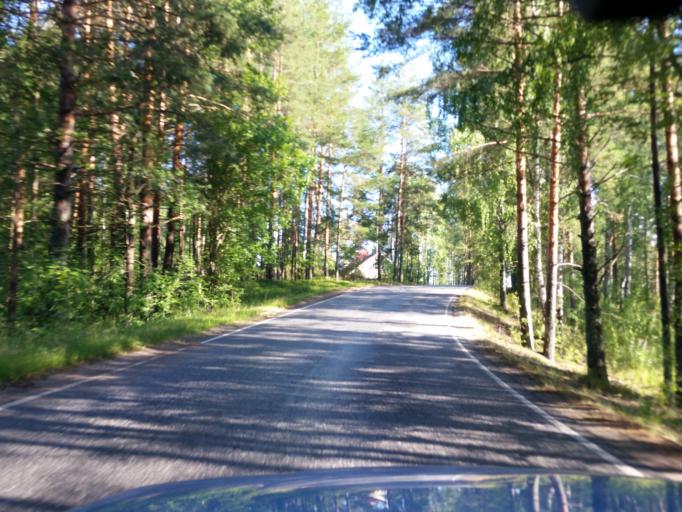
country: FI
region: Southern Savonia
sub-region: Savonlinna
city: Sulkava
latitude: 61.7705
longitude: 28.4338
